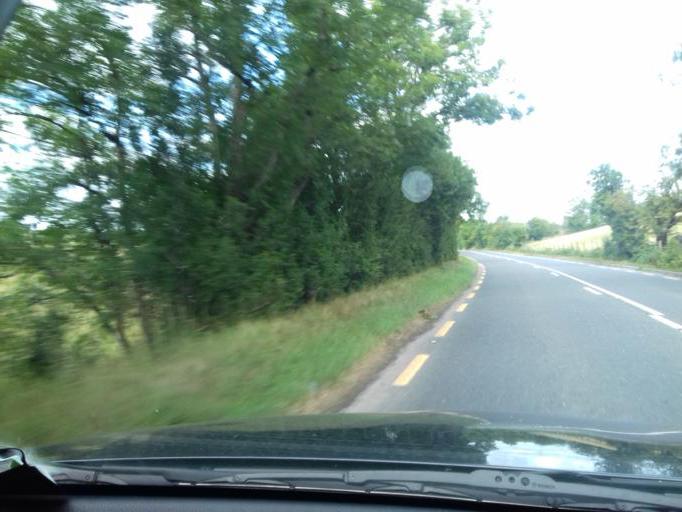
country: IE
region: Leinster
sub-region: Wicklow
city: Valleymount
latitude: 53.0543
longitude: -6.6276
